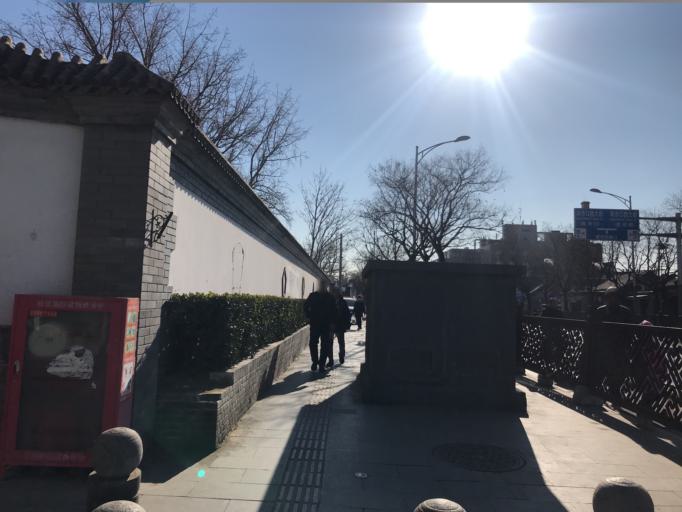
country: CN
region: Beijing
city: Beijing
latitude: 39.8912
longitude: 116.3885
